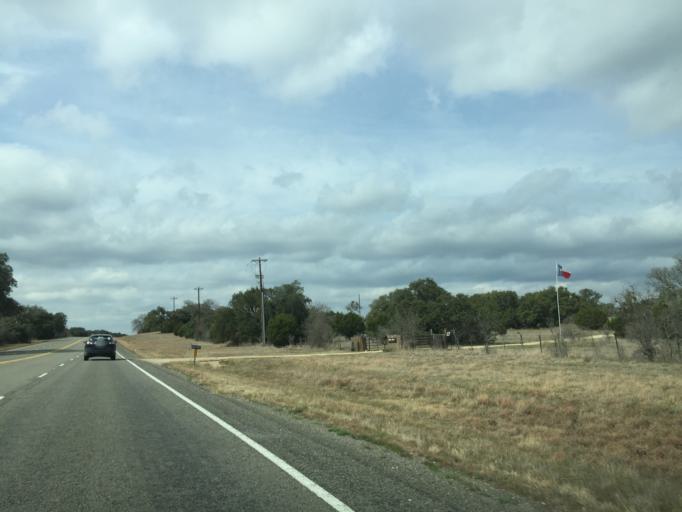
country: US
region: Texas
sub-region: Burnet County
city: Meadowlakes
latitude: 30.4937
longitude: -98.2454
